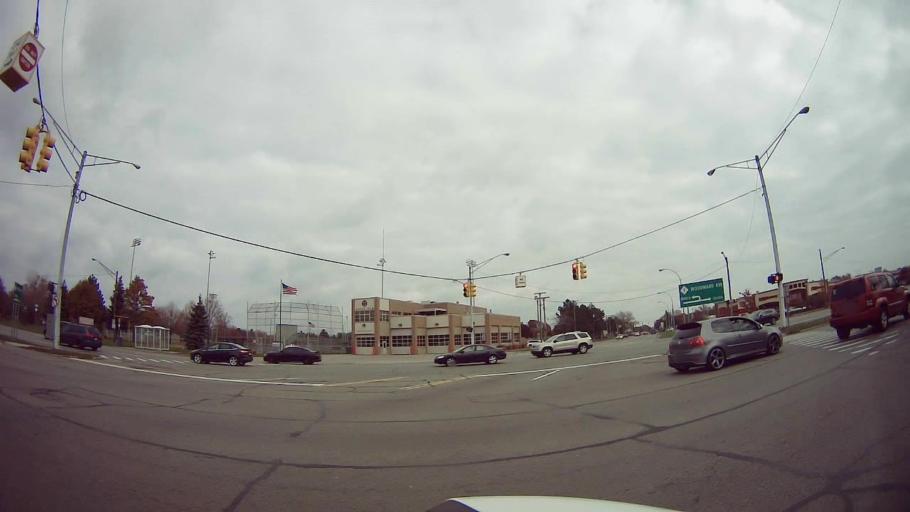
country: US
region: Michigan
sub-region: Oakland County
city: Berkley
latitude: 42.5164
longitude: -83.1846
